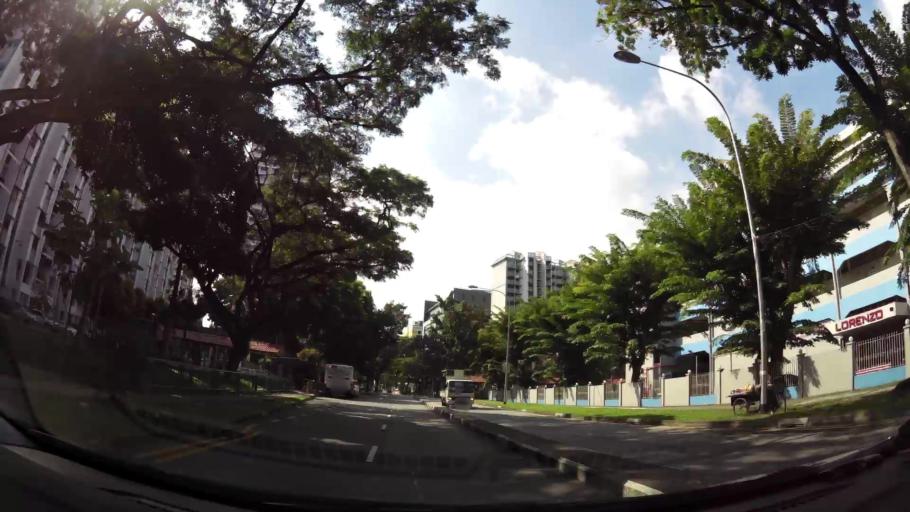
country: SG
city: Singapore
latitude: 1.3176
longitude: 103.8780
